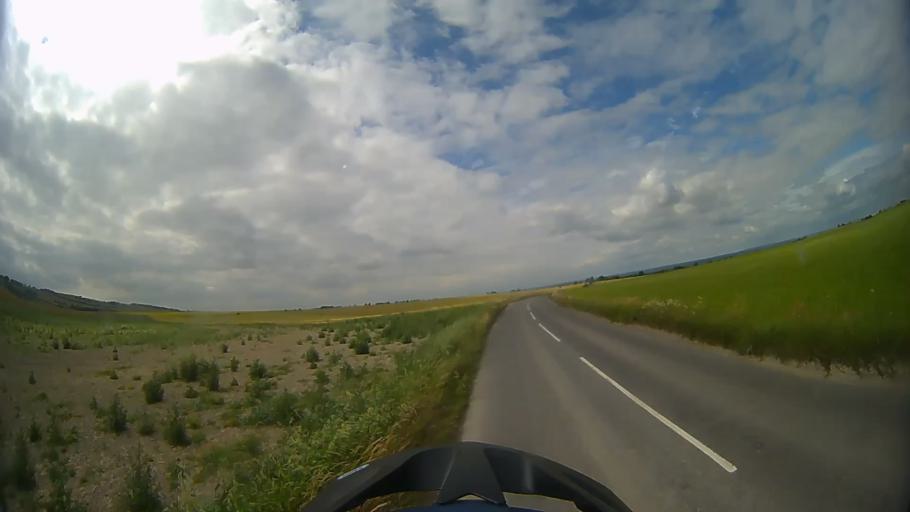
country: GB
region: England
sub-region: Oxfordshire
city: Wantage
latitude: 51.5740
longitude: -1.4800
